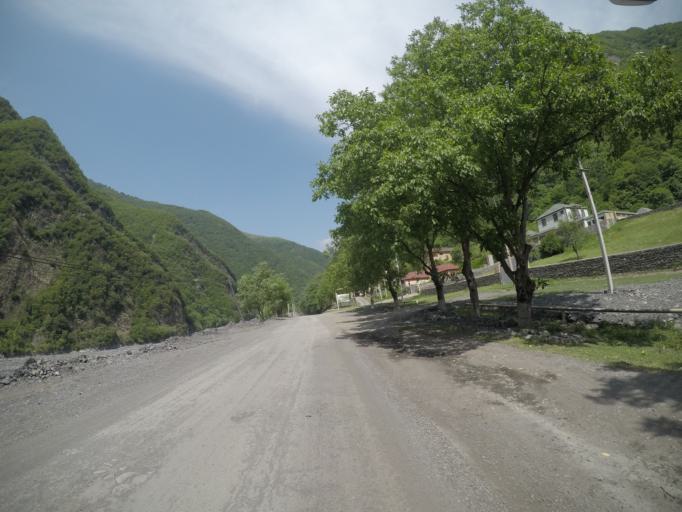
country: AZ
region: Qakh Rayon
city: Qaxbas
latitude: 41.4612
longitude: 47.0299
